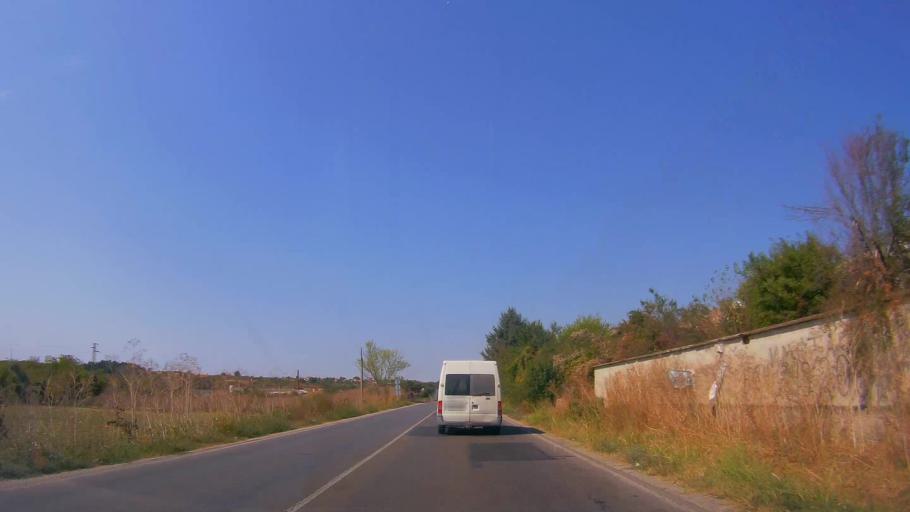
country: BG
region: Razgrad
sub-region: Obshtina Tsar Kaloyan
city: Tsar Kaloyan
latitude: 43.5995
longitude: 26.2471
